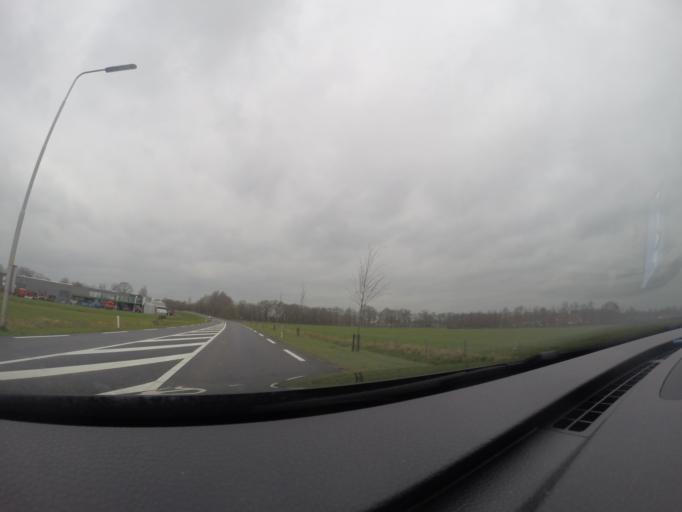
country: NL
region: Gelderland
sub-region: Berkelland
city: Borculo
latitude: 52.1274
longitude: 6.5310
